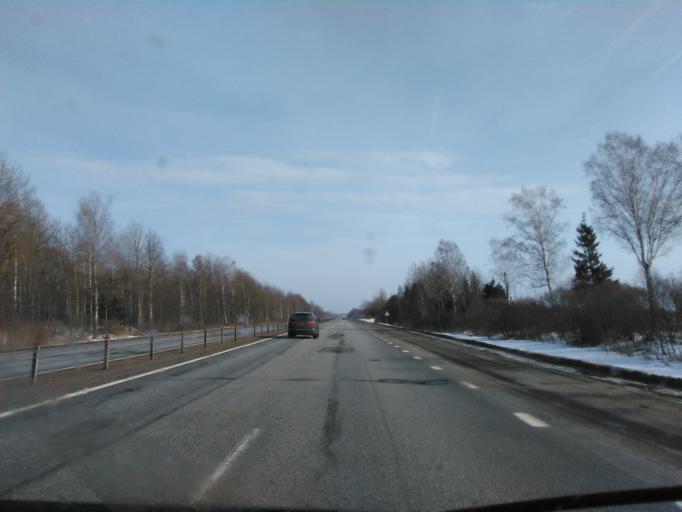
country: BY
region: Vitebsk
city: Dubrowna
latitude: 54.6857
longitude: 30.8257
